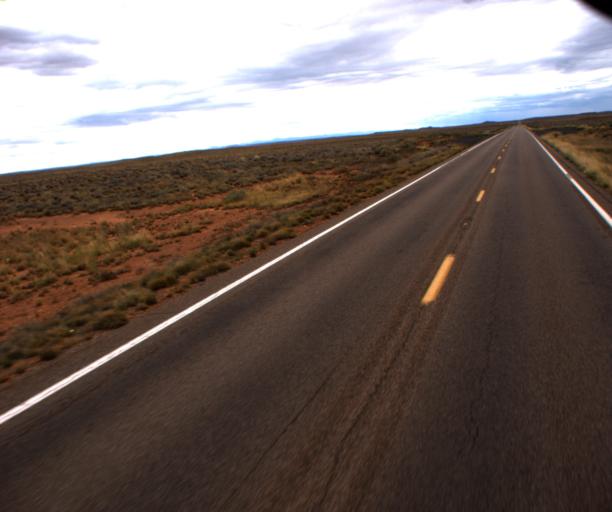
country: US
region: Arizona
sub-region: Navajo County
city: Holbrook
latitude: 34.7898
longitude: -110.1325
